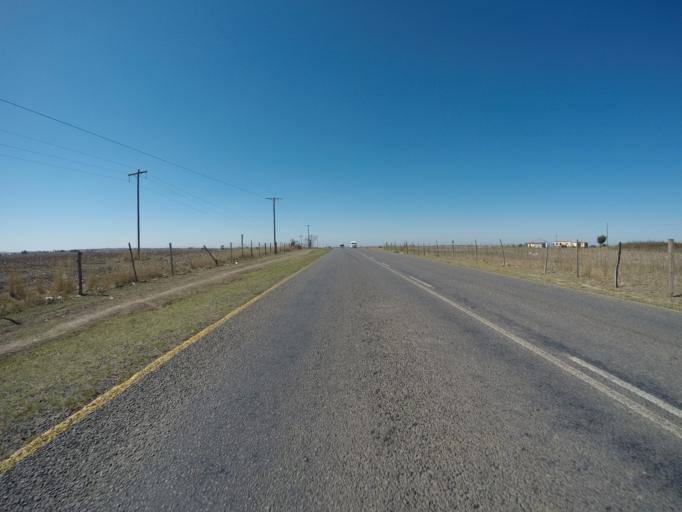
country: ZA
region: Eastern Cape
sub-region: OR Tambo District Municipality
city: Mthatha
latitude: -31.8880
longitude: 28.7624
